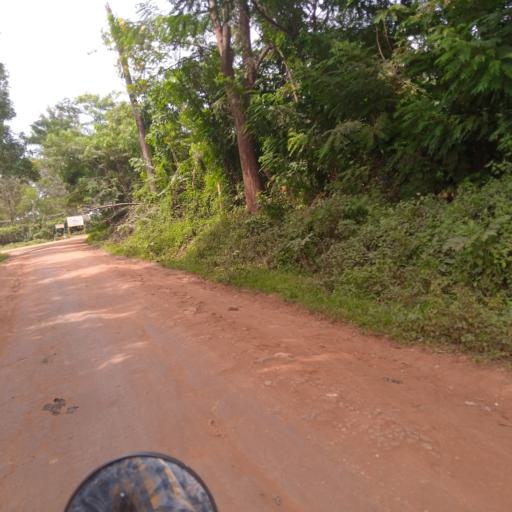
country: UG
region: Eastern Region
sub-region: Mbale District
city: Mbale
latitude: 1.0924
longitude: 34.1874
